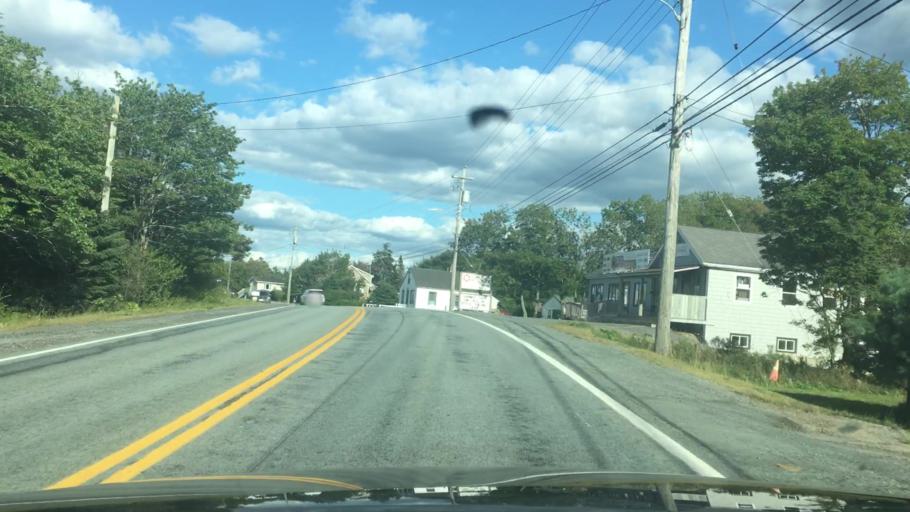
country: CA
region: Nova Scotia
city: Halifax
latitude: 44.6006
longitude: -63.6782
